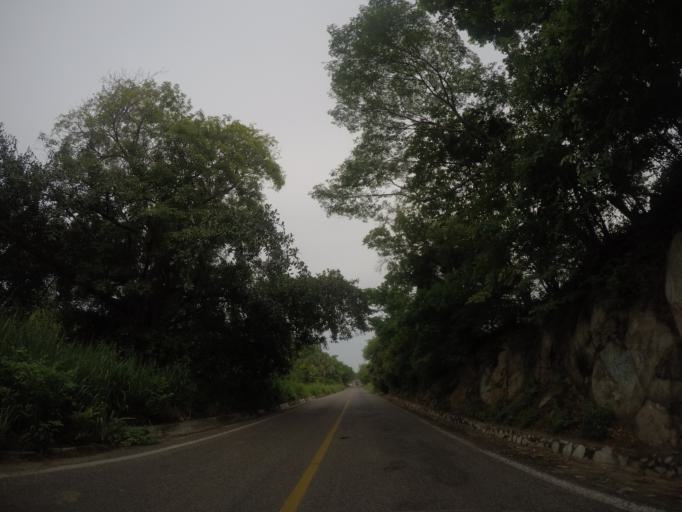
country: MX
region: Oaxaca
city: San Pedro Mixtepec
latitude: 15.9551
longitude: -97.2042
